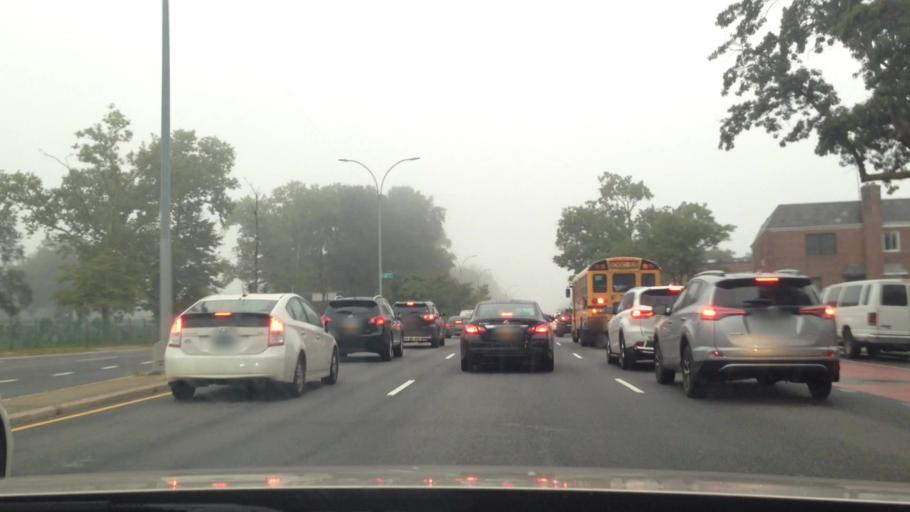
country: US
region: New York
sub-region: Queens County
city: Borough of Queens
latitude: 40.7169
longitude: -73.8620
